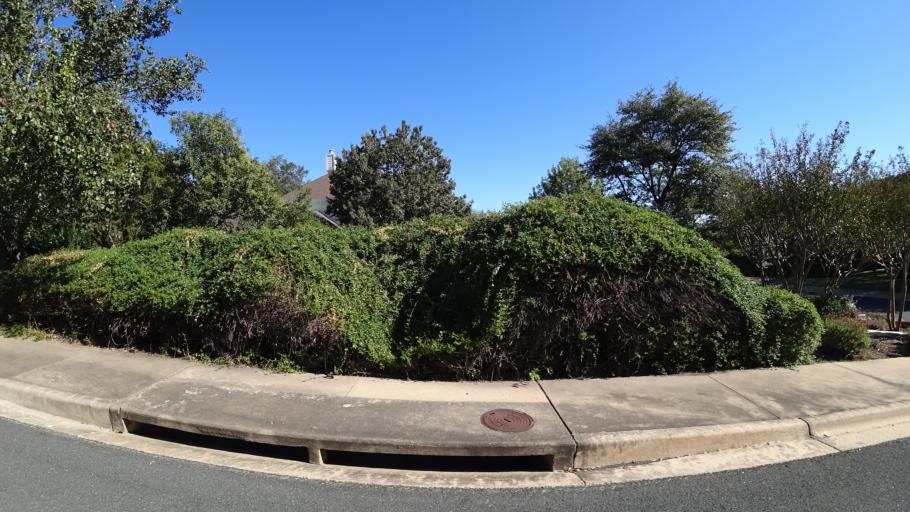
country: US
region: Texas
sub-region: Travis County
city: West Lake Hills
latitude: 30.3297
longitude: -97.7947
